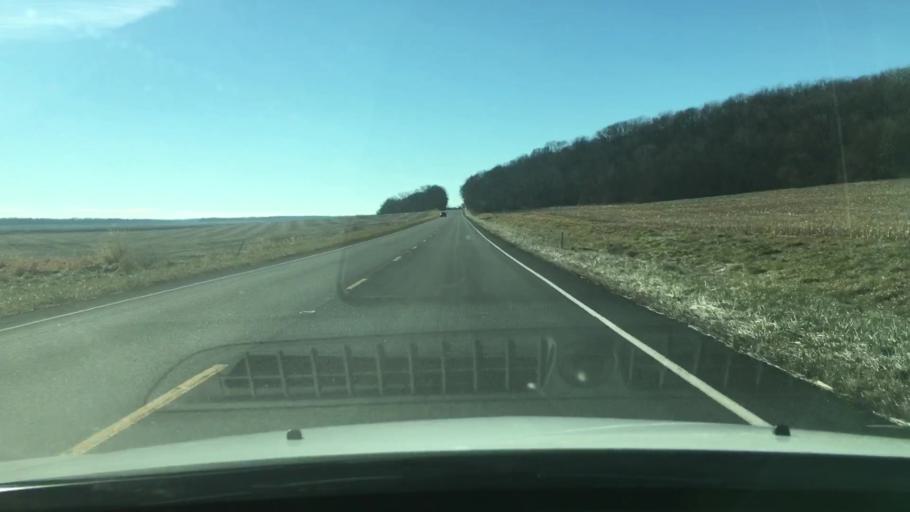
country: US
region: Illinois
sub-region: Fulton County
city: Canton
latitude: 40.4373
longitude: -89.9693
